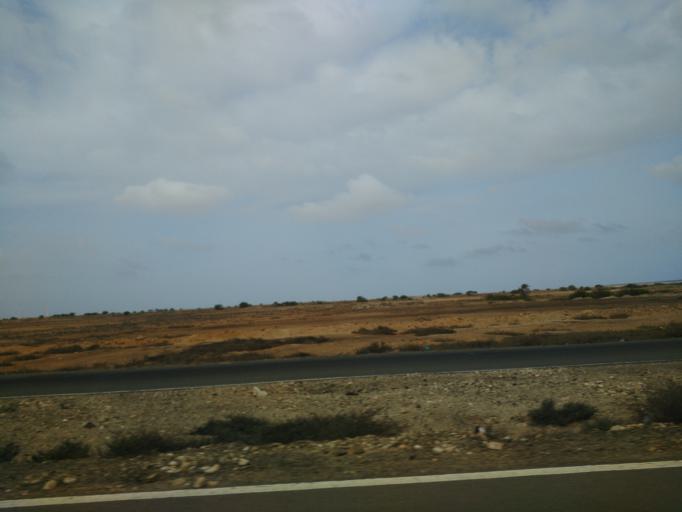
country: CV
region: Sal
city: Espargos
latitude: 16.6798
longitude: -22.9339
